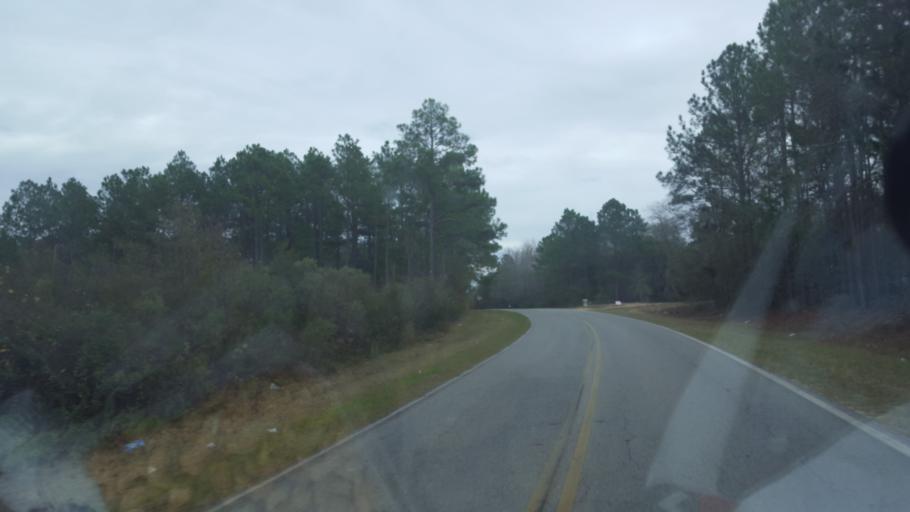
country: US
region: Georgia
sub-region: Ben Hill County
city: Fitzgerald
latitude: 31.7525
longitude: -83.3372
